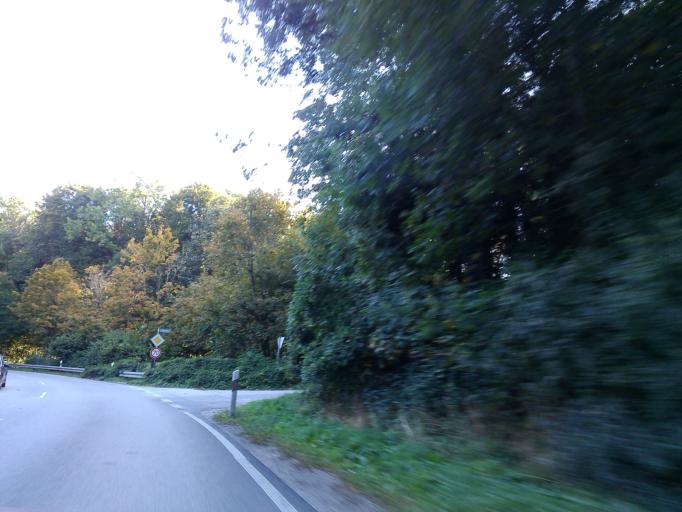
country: DE
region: Bavaria
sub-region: Upper Bavaria
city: Fuerstenfeldbruck
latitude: 48.1699
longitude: 11.2690
